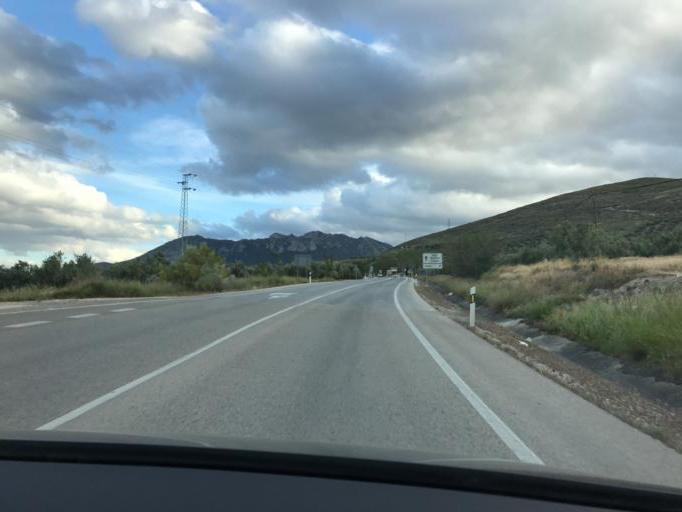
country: ES
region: Andalusia
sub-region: Provincia de Jaen
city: Jodar
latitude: 37.8581
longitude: -3.3512
